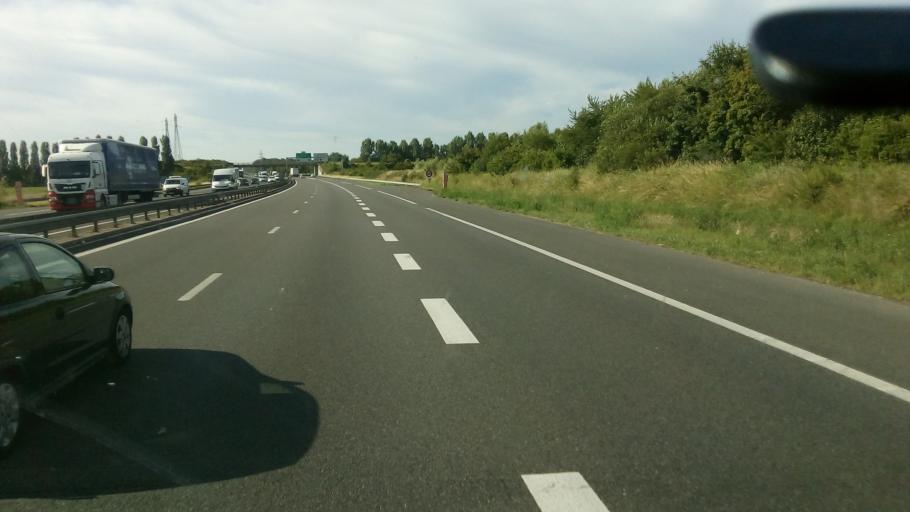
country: FR
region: Ile-de-France
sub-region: Departement de Seine-et-Marne
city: Vert-Saint-Denis
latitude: 48.5780
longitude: 2.6381
